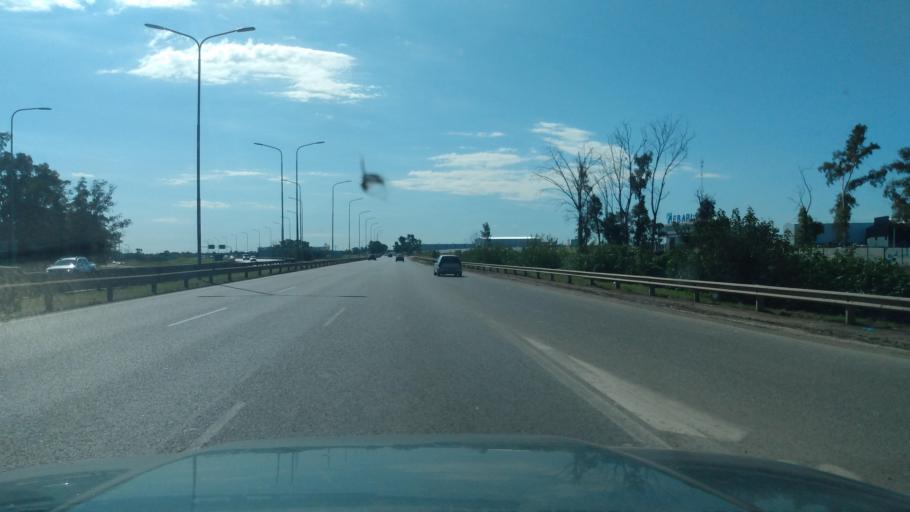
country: AR
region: Buenos Aires
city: Hurlingham
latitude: -34.5306
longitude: -58.5946
